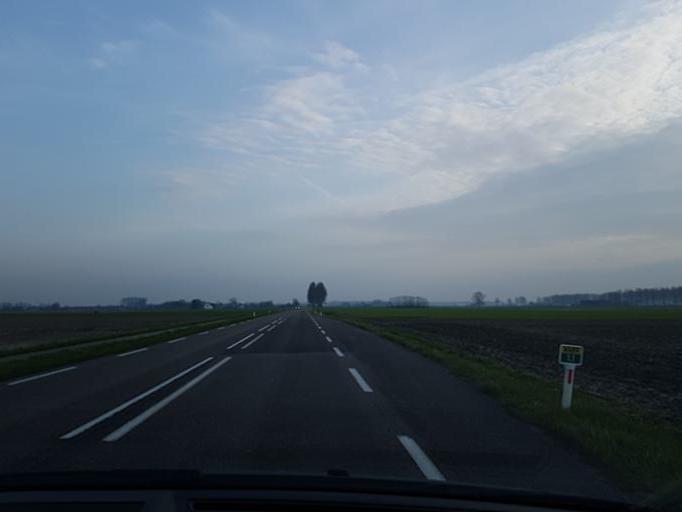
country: NL
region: Zeeland
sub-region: Gemeente Hulst
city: Hulst
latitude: 51.3270
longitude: 4.0333
